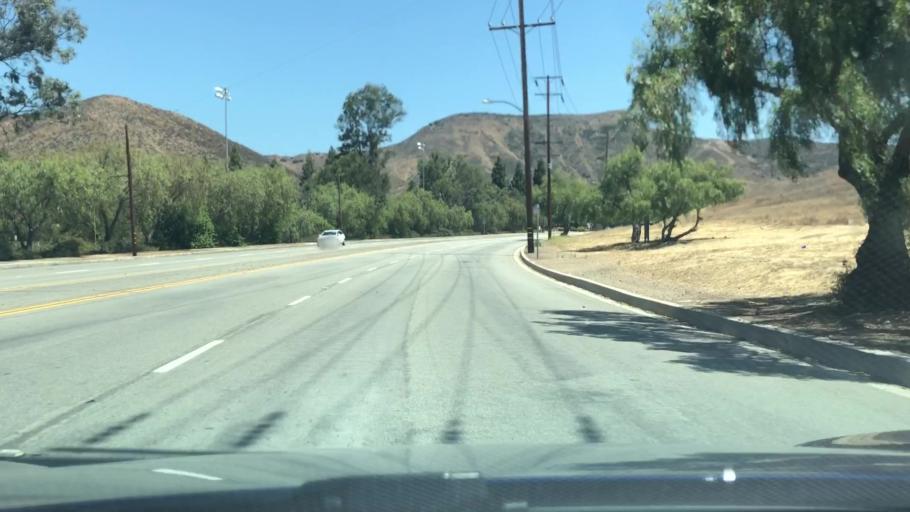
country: US
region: California
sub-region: Ventura County
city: Casa Conejo
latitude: 34.1900
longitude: -118.9541
